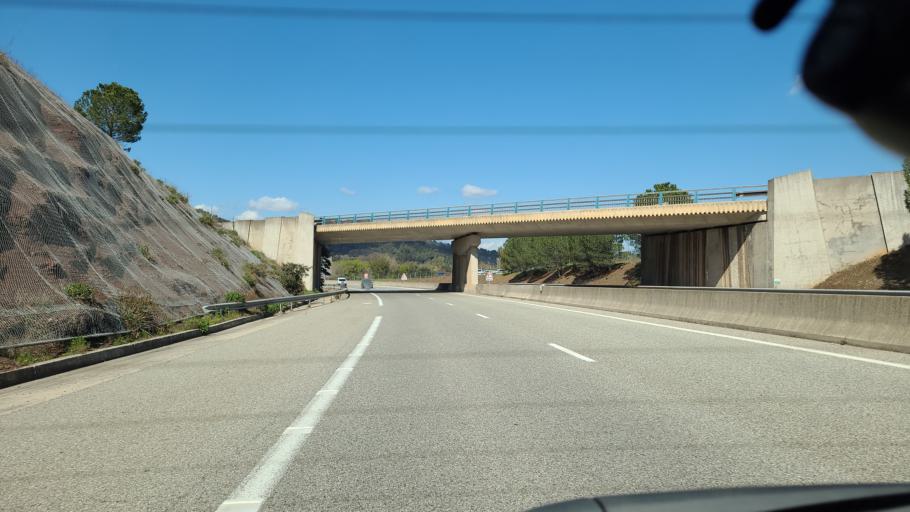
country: FR
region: Provence-Alpes-Cote d'Azur
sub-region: Departement du Var
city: Le Cannet-des-Maures
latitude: 43.3860
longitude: 6.3584
